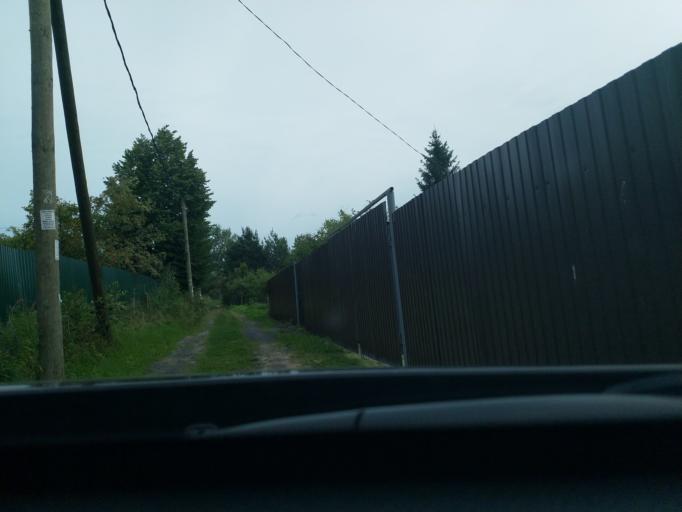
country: RU
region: Leningrad
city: Nikol'skoye
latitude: 59.7259
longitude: 30.7669
